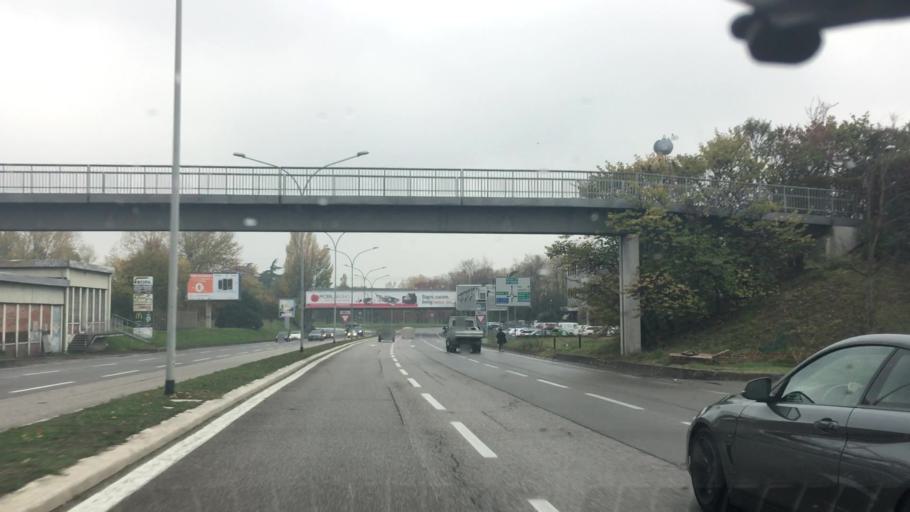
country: IT
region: Emilia-Romagna
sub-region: Provincia di Bologna
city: Casalecchio di Reno
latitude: 44.5085
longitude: 11.2798
